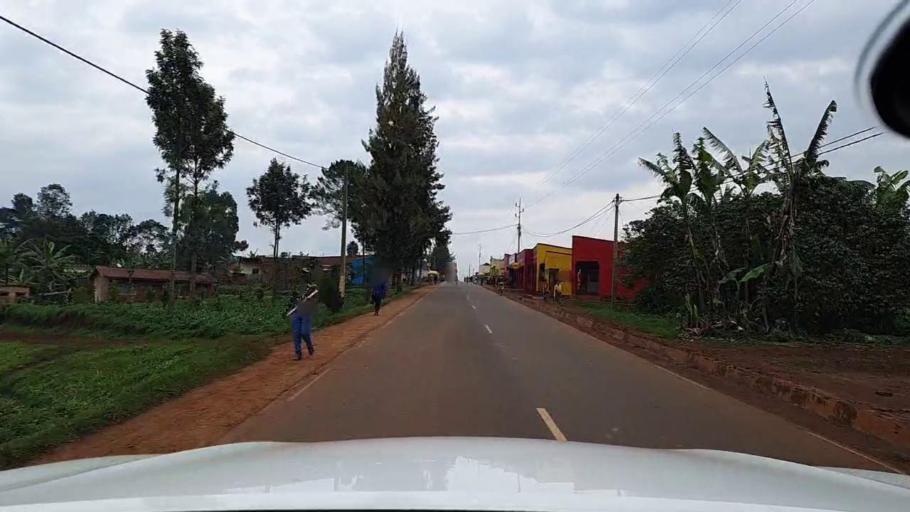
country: RW
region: Western Province
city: Cyangugu
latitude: -2.6349
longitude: 28.9521
